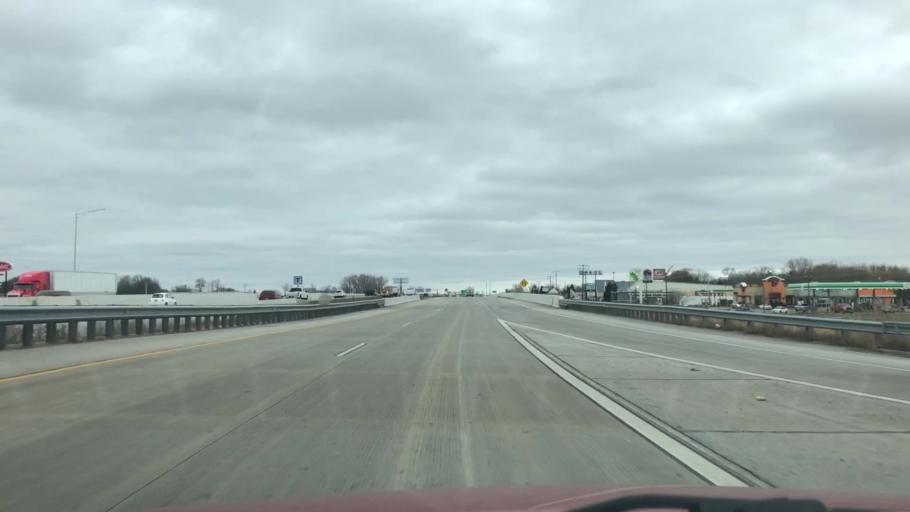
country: US
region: Wisconsin
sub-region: Brown County
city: De Pere
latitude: 44.4537
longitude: -88.0897
